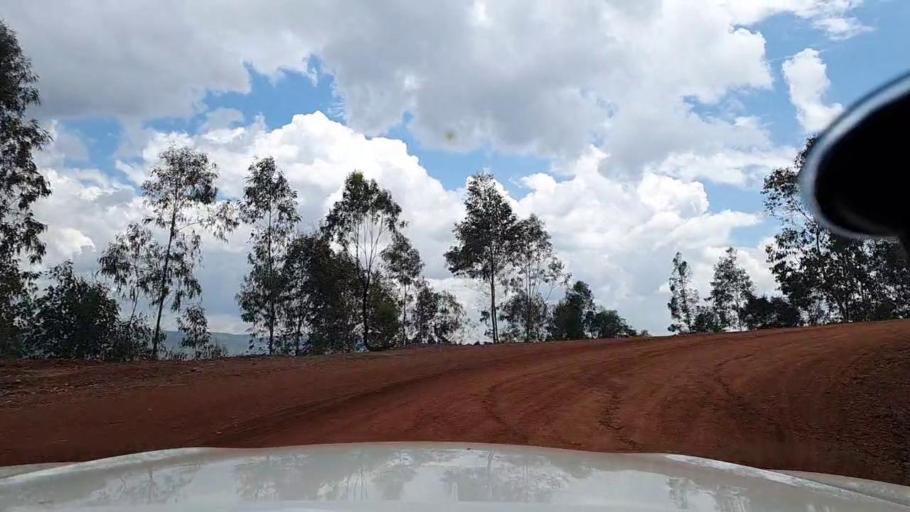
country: RW
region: Northern Province
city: Byumba
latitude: -1.7554
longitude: 29.8472
